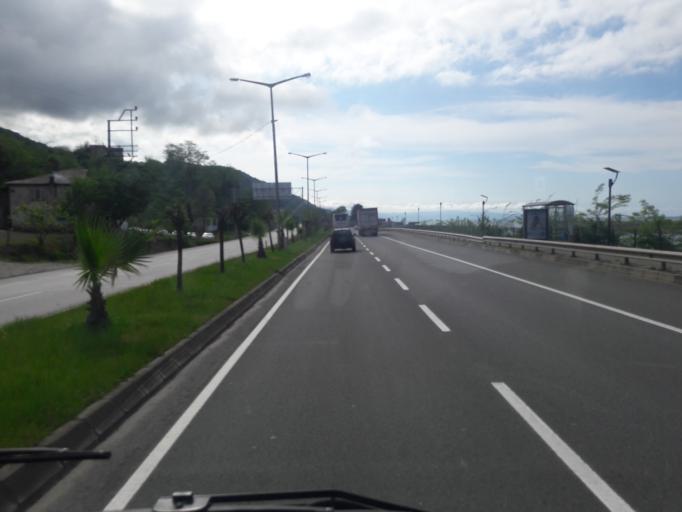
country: TR
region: Ordu
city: Gulyali
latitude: 40.9652
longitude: 38.0710
